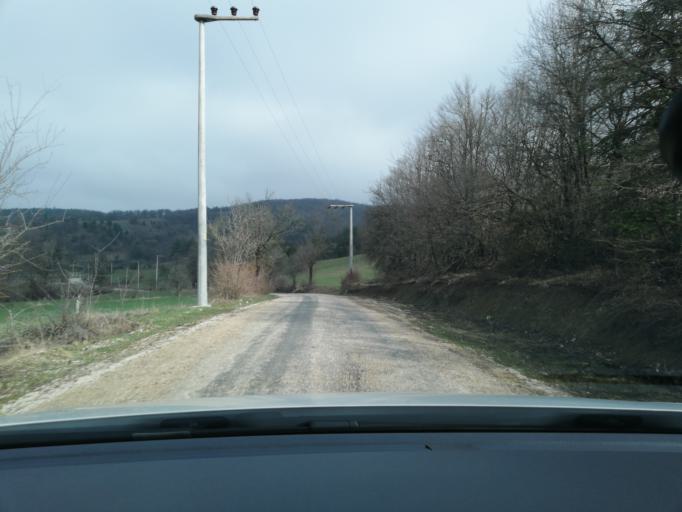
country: TR
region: Bolu
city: Bolu
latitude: 40.6786
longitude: 31.4738
